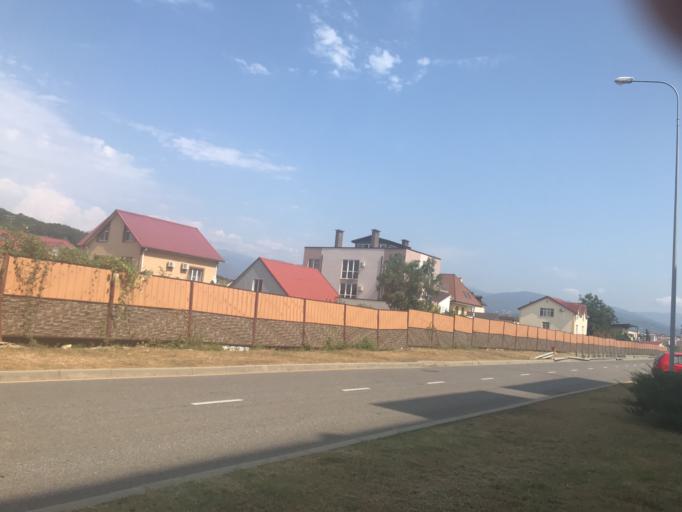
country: RU
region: Krasnodarskiy
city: Vysokoye
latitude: 43.4035
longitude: 39.9851
